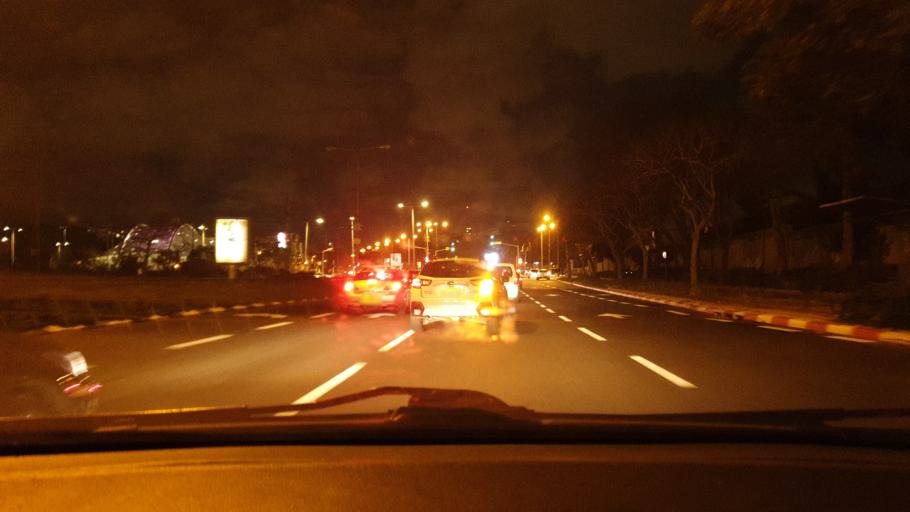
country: IL
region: Central District
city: Rishon LeZiyyon
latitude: 31.9526
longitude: 34.8026
